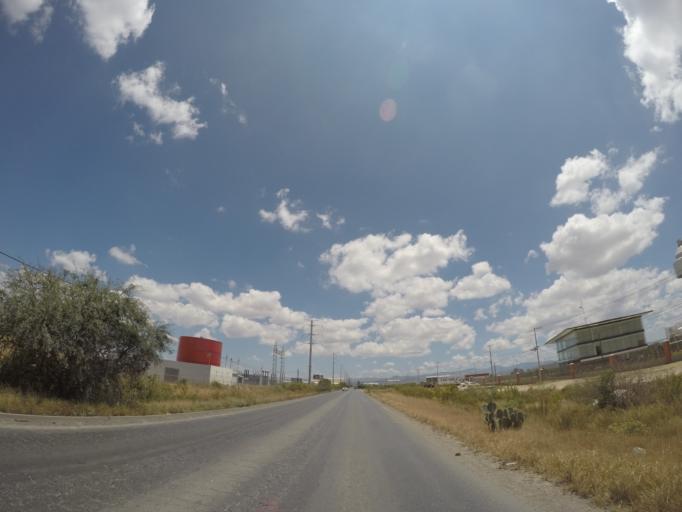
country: MX
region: San Luis Potosi
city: La Pila
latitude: 22.0446
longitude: -100.8795
